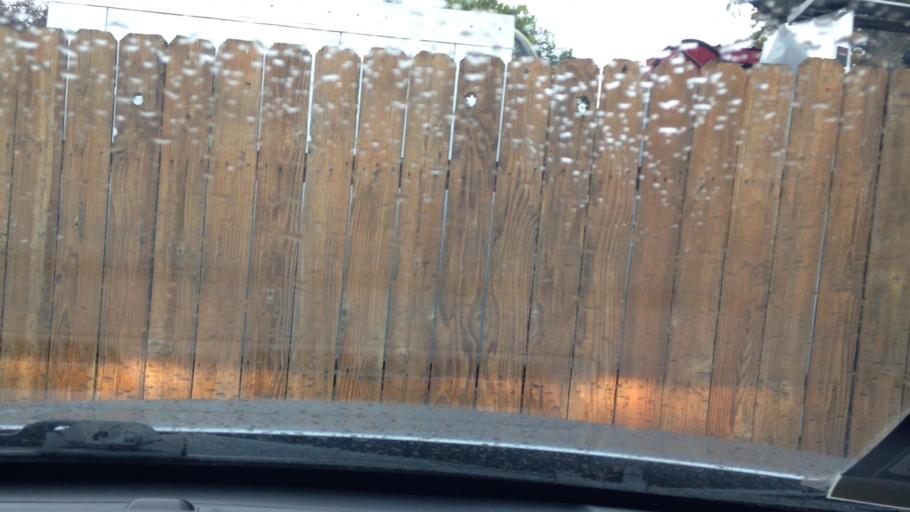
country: US
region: Kansas
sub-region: Leavenworth County
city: Lansing
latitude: 39.2739
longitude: -94.9006
